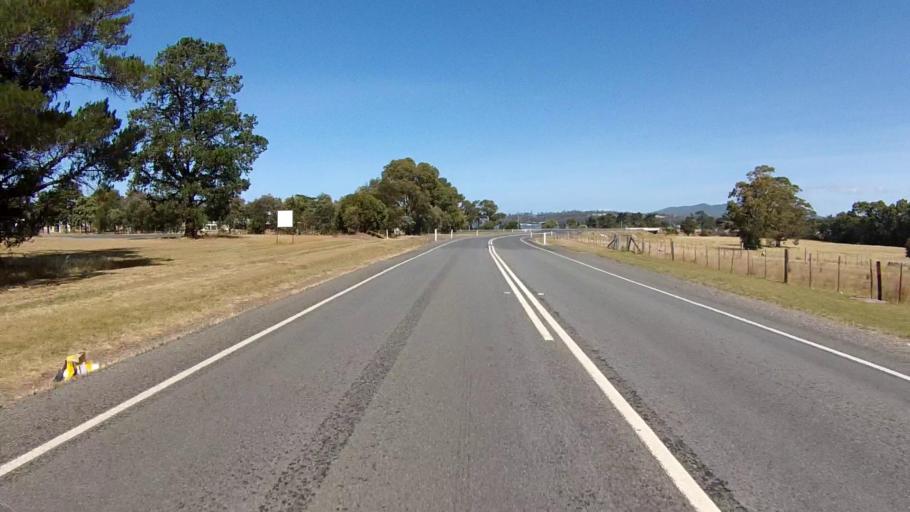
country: AU
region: Tasmania
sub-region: Sorell
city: Sorell
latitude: -42.5060
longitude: 147.9085
